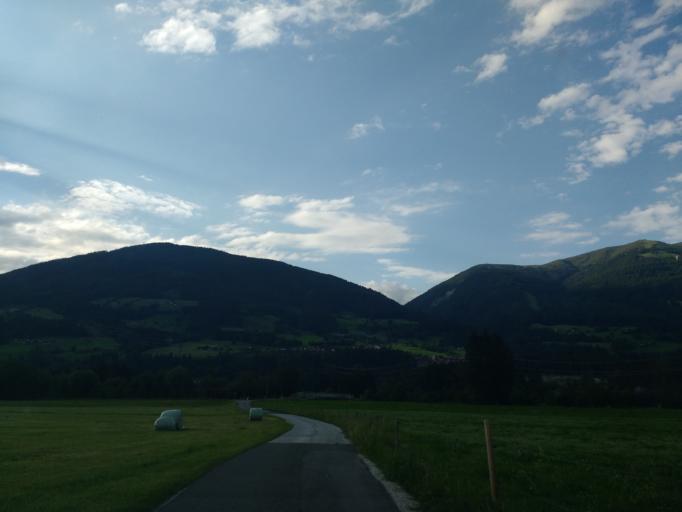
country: AT
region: Salzburg
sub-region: Politischer Bezirk Zell am See
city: Neukirchen am Grossvenediger
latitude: 47.2405
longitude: 12.2616
